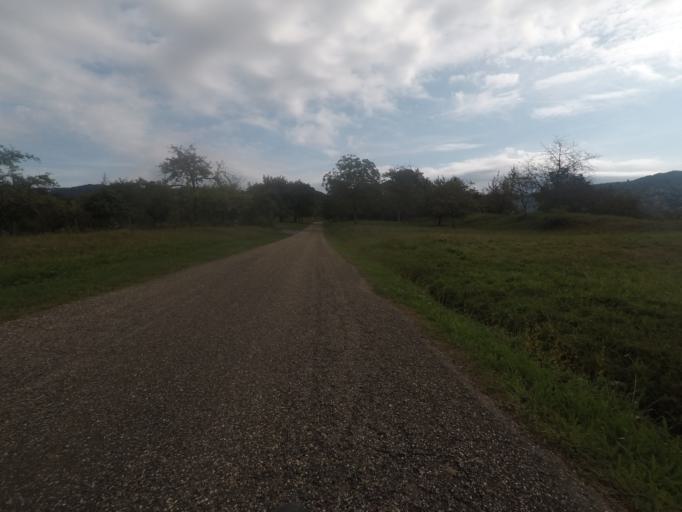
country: DE
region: Baden-Wuerttemberg
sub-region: Karlsruhe Region
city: Gaggenau
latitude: 48.8071
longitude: 8.3548
